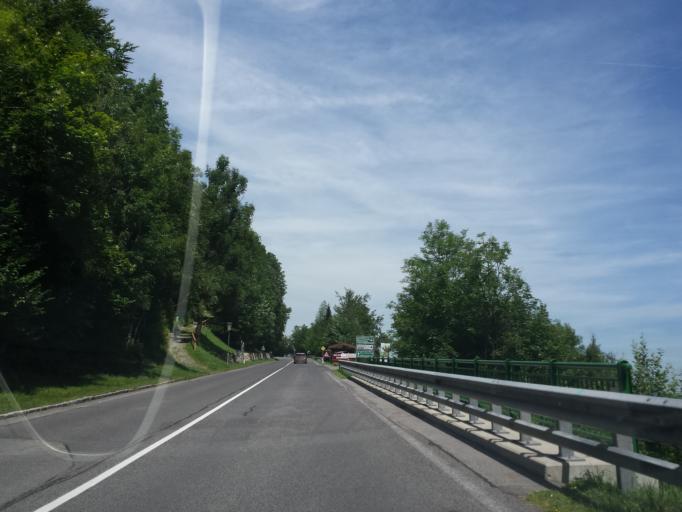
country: AT
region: Lower Austria
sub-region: Politischer Bezirk Neunkirchen
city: Semmering
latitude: 47.6336
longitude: 15.8333
